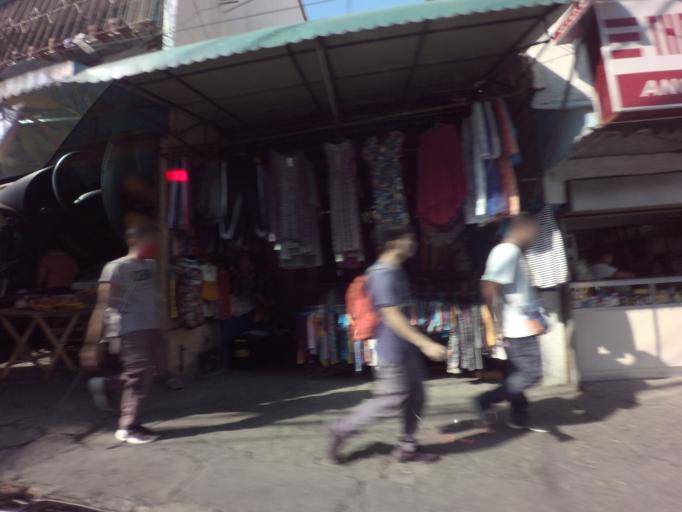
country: PH
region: Calabarzon
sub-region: Province of Rizal
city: Taguig
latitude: 14.5004
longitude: 121.0513
